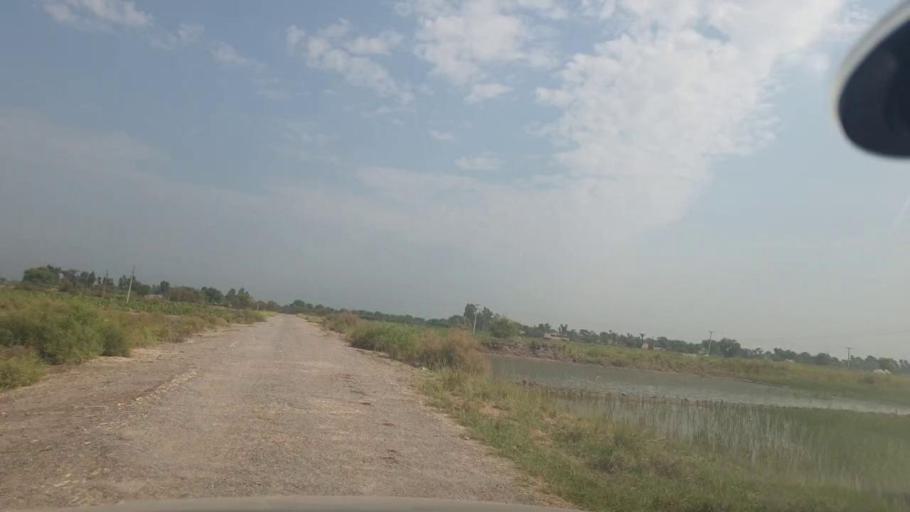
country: PK
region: Balochistan
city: Mehrabpur
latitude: 28.0564
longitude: 68.1240
